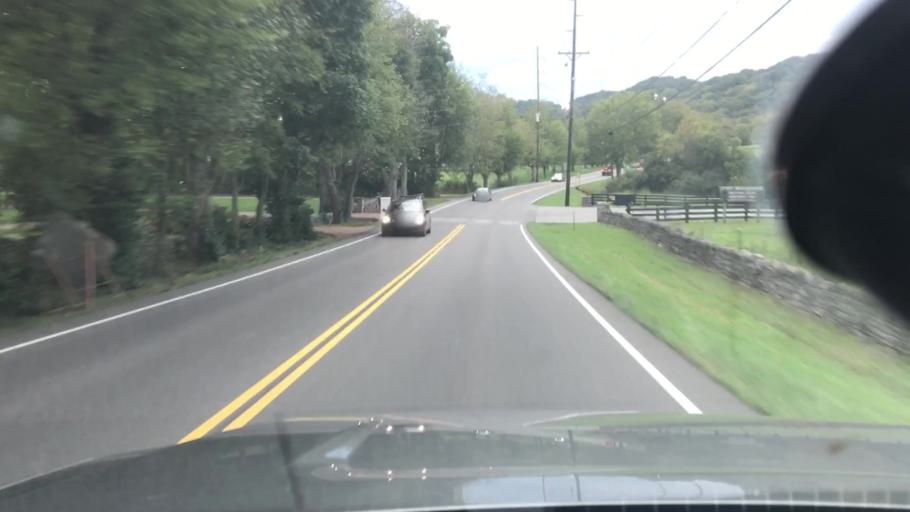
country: US
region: Tennessee
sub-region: Davidson County
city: Forest Hills
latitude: 36.0522
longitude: -86.8926
